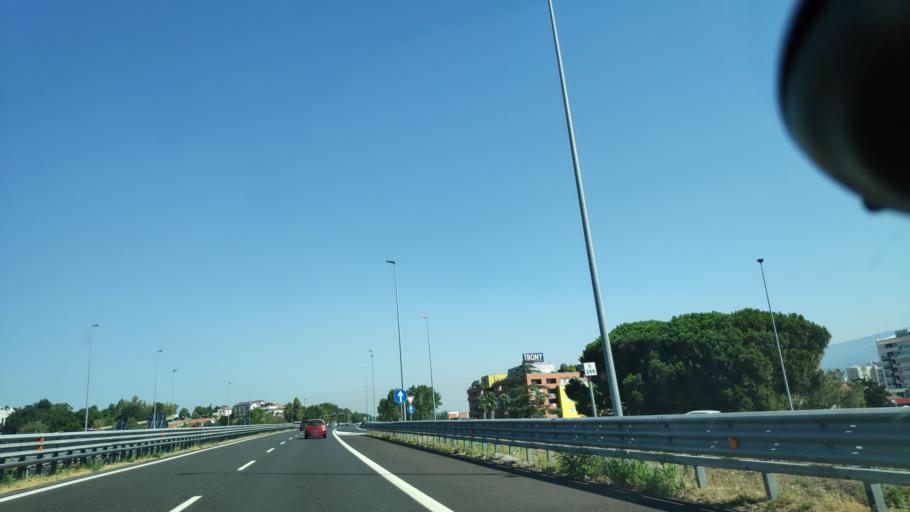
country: IT
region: Calabria
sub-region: Provincia di Cosenza
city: Quattromiglia
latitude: 39.3513
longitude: 16.2340
